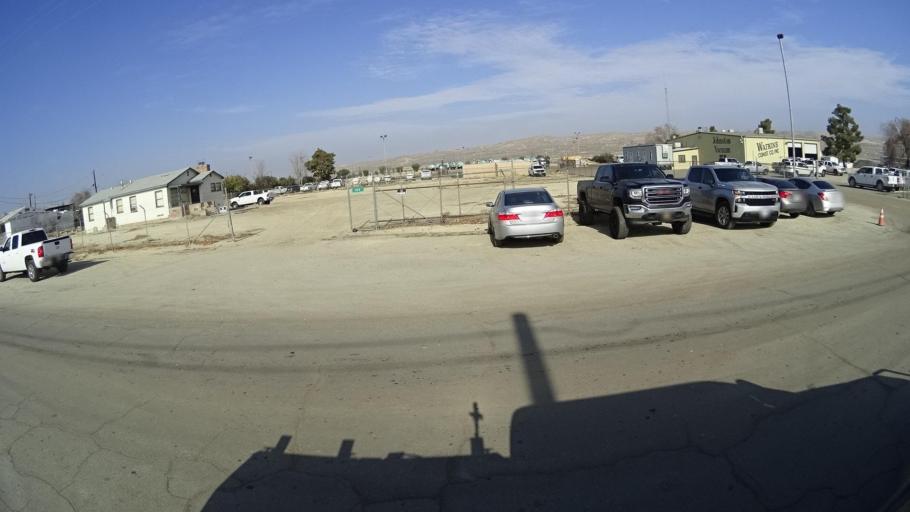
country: US
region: California
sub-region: Kern County
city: Ford City
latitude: 35.1546
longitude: -119.4463
